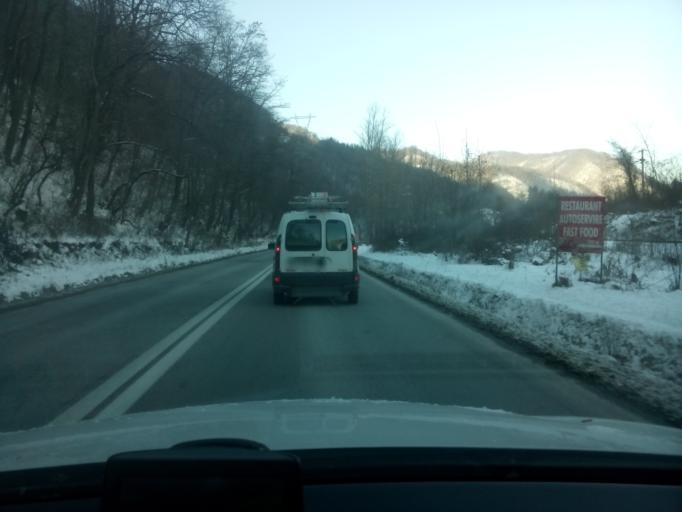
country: RO
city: Cainenii Mici
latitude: 45.5193
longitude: 24.2739
